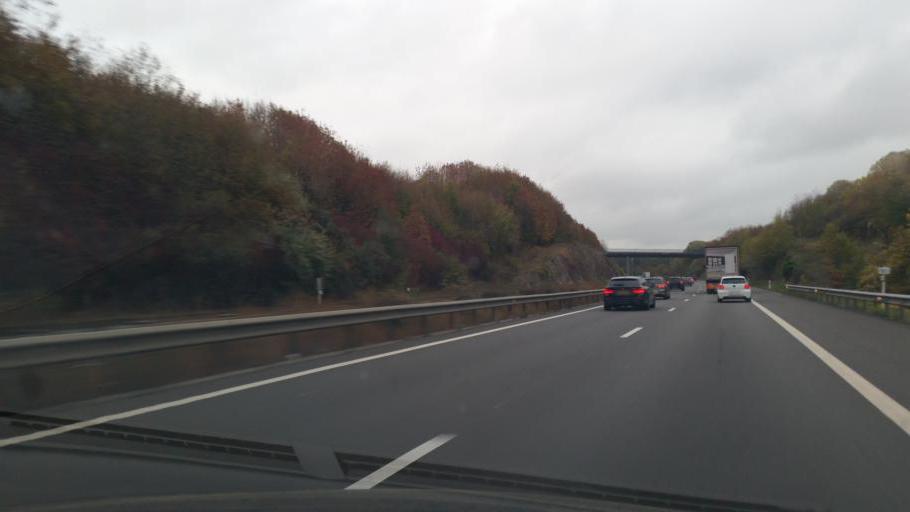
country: LU
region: Grevenmacher
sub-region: Canton de Grevenmacher
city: Flaxweiler
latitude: 49.6425
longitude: 6.3081
